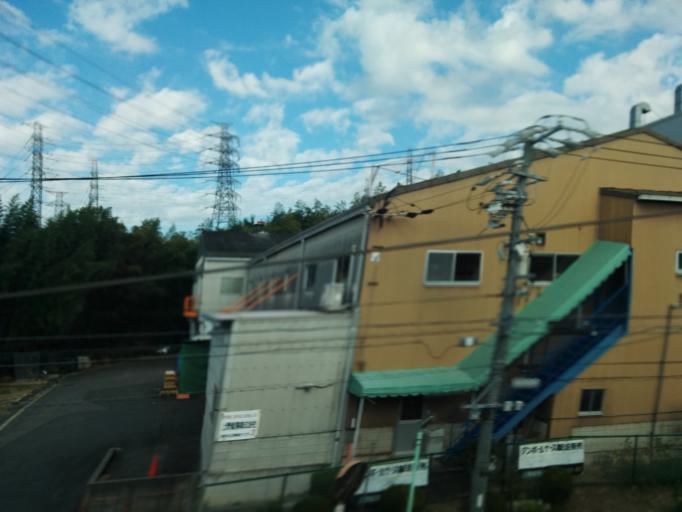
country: JP
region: Aichi
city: Obu
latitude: 35.0531
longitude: 136.9505
